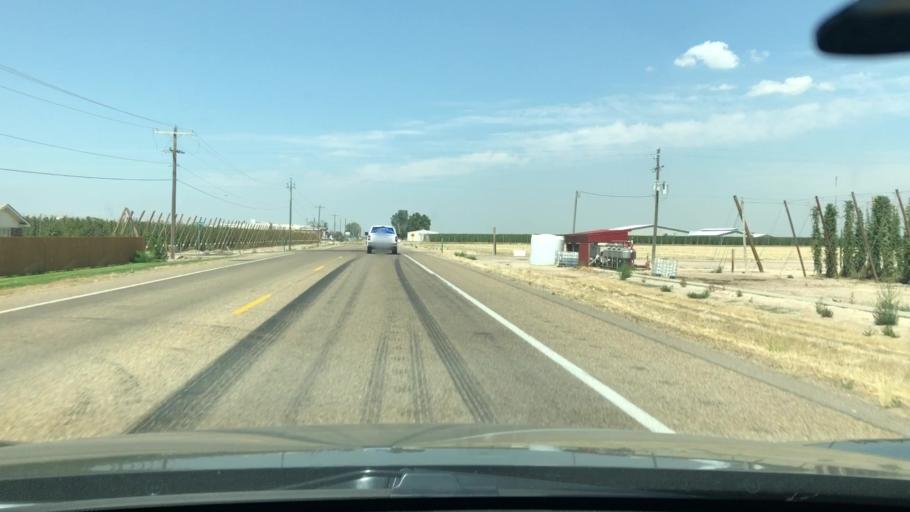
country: US
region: Idaho
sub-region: Canyon County
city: Wilder
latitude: 43.6899
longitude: -116.9120
